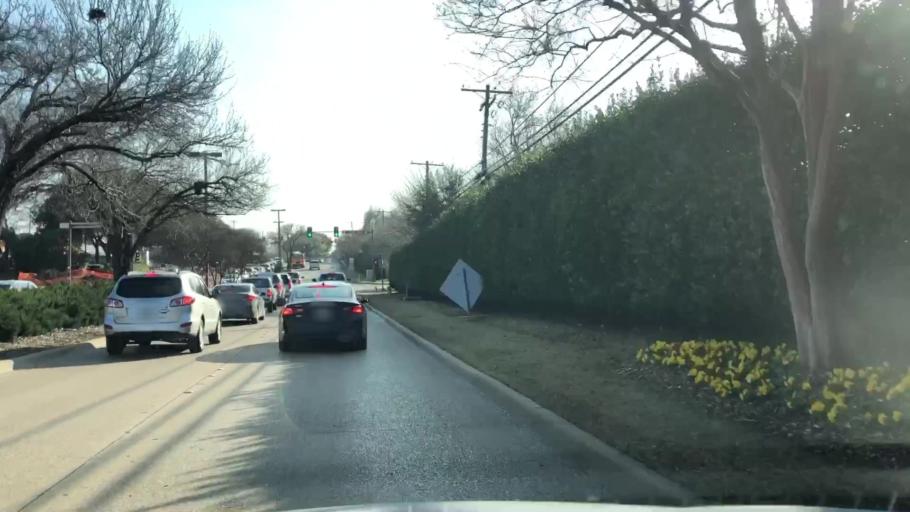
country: US
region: Texas
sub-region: Dallas County
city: Addison
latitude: 32.9422
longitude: -96.8558
